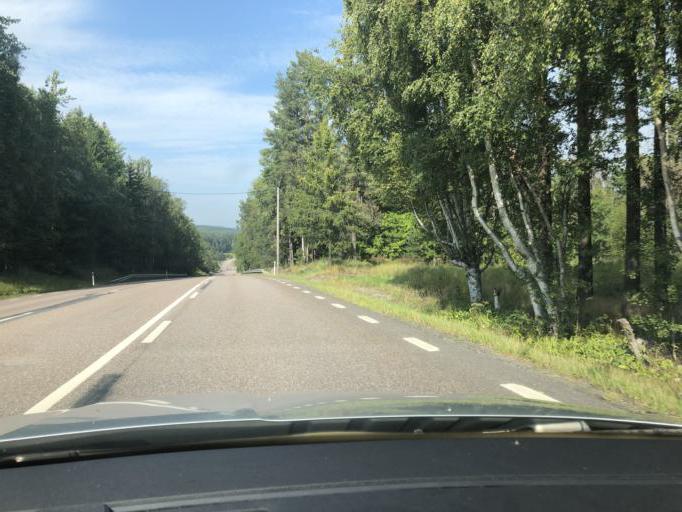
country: SE
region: Vaesternorrland
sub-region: Kramfors Kommun
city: Kramfors
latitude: 62.8150
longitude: 17.8640
